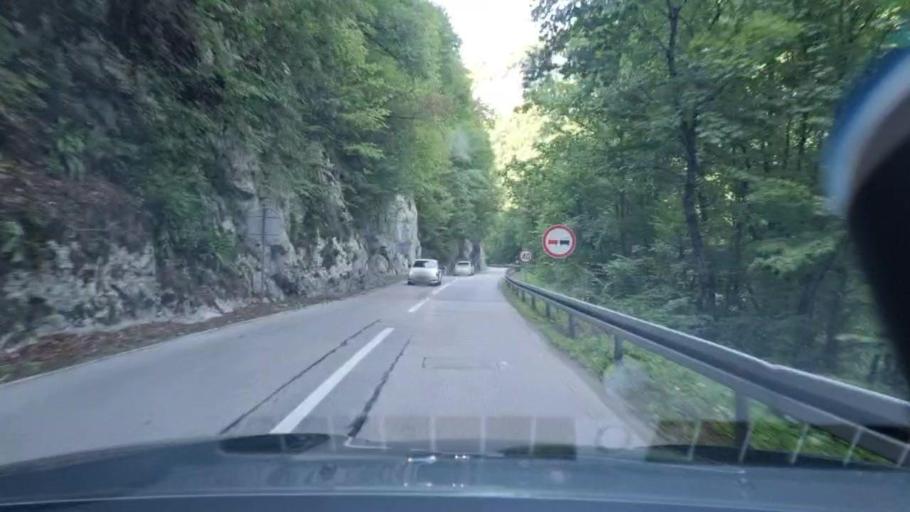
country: BA
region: Federation of Bosnia and Herzegovina
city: Bosanska Krupa
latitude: 44.8690
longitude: 16.0875
